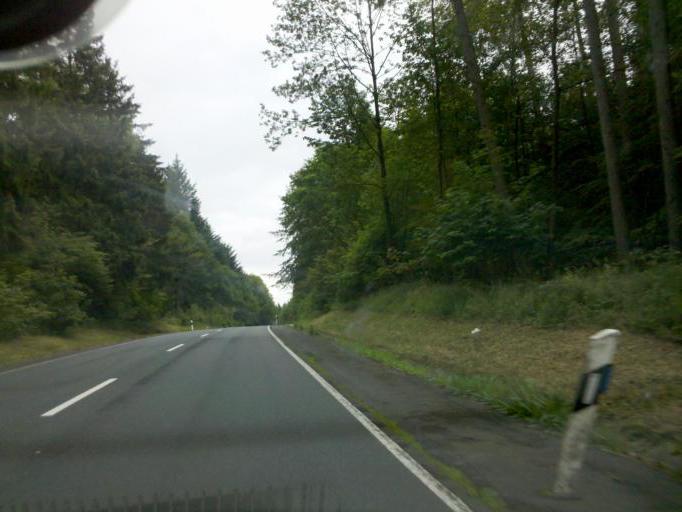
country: DE
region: North Rhine-Westphalia
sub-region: Regierungsbezirk Arnsberg
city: Wilnsdorf
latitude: 50.8500
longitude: 8.0691
